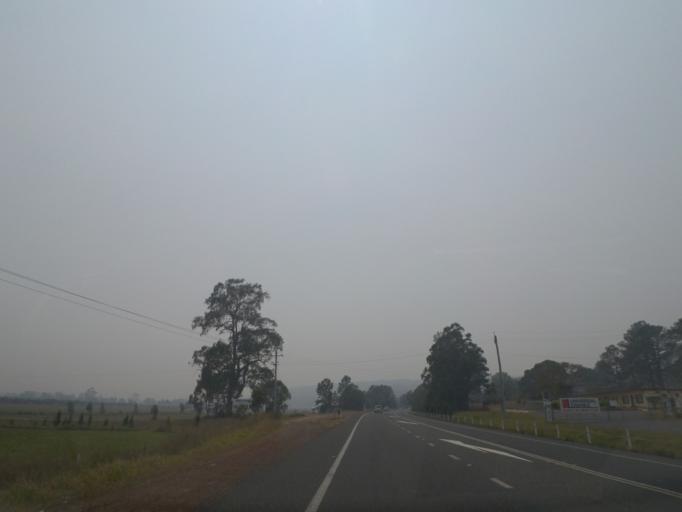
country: AU
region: New South Wales
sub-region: Clarence Valley
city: Maclean
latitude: -29.5653
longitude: 153.1390
